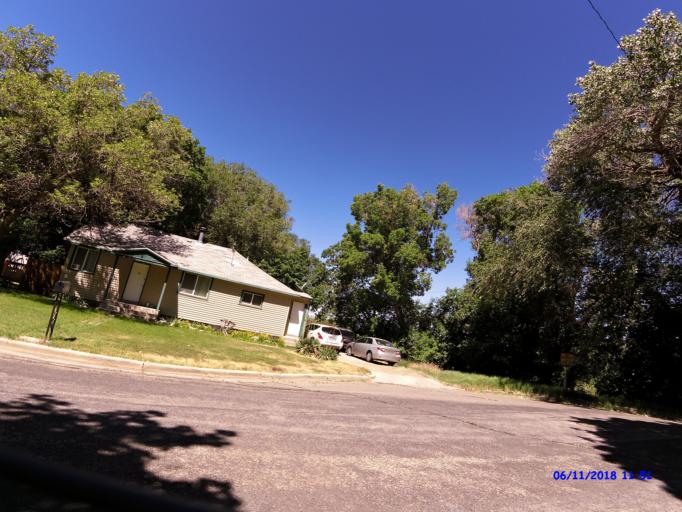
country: US
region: Utah
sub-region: Weber County
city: Ogden
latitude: 41.2337
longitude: -111.9520
